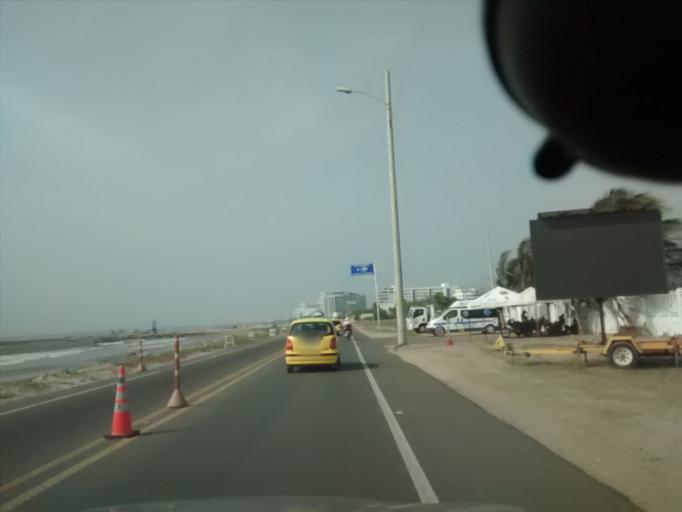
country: CO
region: Bolivar
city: Cartagena
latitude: 10.4533
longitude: -75.5139
